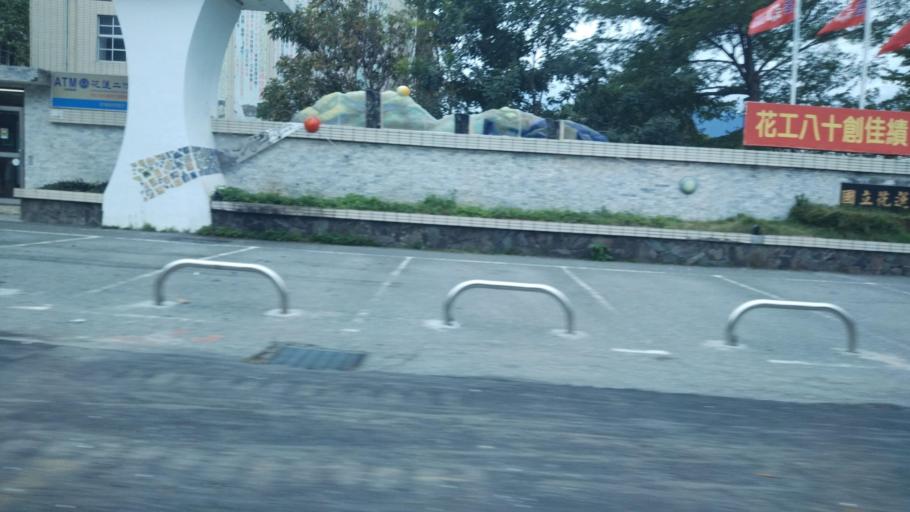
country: TW
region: Taiwan
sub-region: Hualien
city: Hualian
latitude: 23.9986
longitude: 121.6208
